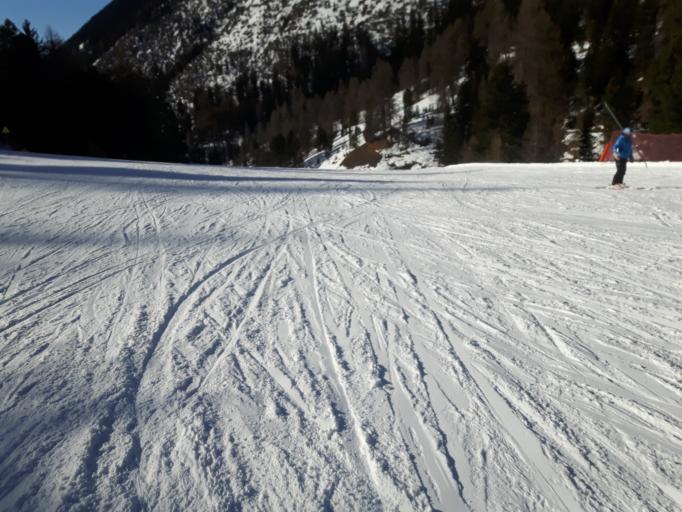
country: IT
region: Trentino-Alto Adige
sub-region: Provincia di Trento
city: Panchia
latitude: 46.3425
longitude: 11.5463
